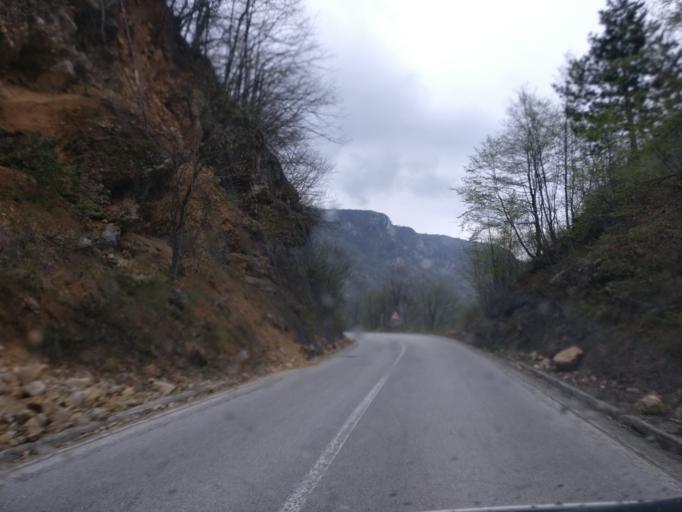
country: ME
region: Opstina Pluzine
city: Pluzine
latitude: 43.2209
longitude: 18.8497
